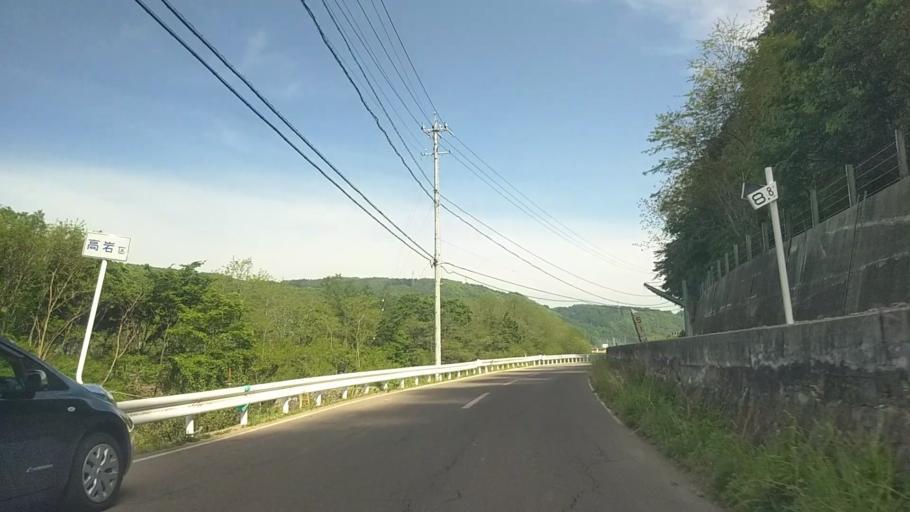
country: JP
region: Nagano
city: Saku
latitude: 36.1098
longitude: 138.4803
